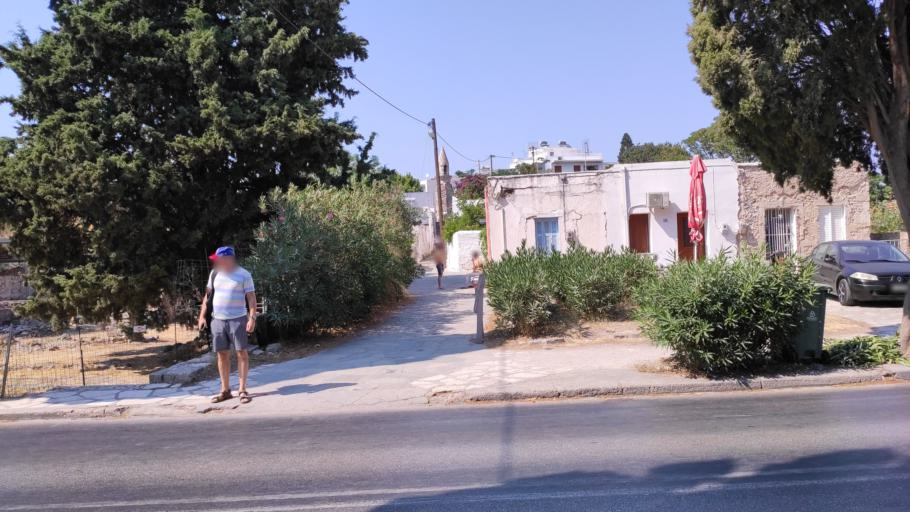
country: GR
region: South Aegean
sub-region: Nomos Dodekanisou
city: Kos
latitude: 36.8902
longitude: 27.2862
